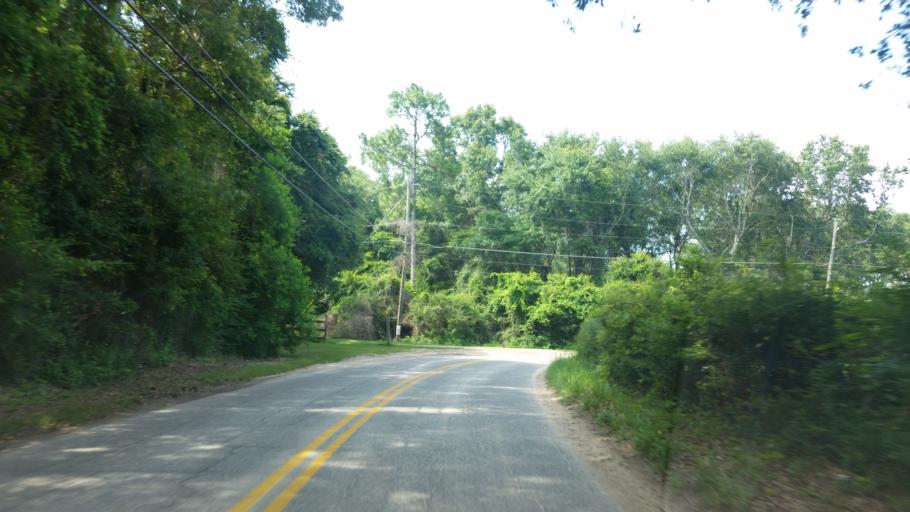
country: US
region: Florida
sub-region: Escambia County
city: Cantonment
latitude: 30.5743
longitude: -87.3623
